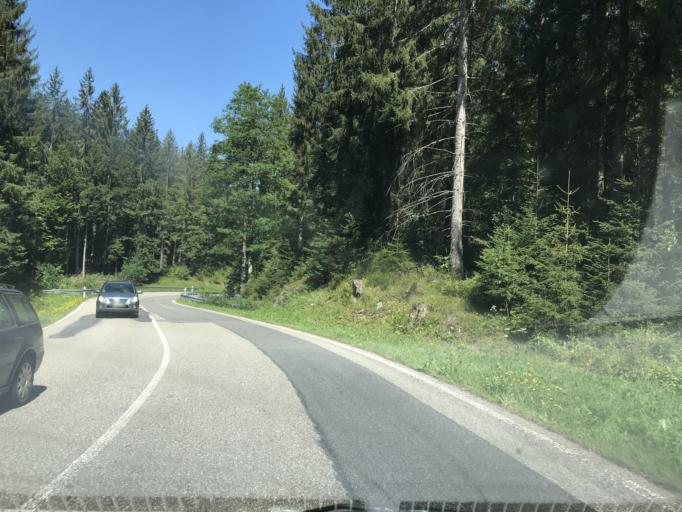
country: DE
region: Baden-Wuerttemberg
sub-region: Freiburg Region
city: Wieden
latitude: 47.8848
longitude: 7.9191
